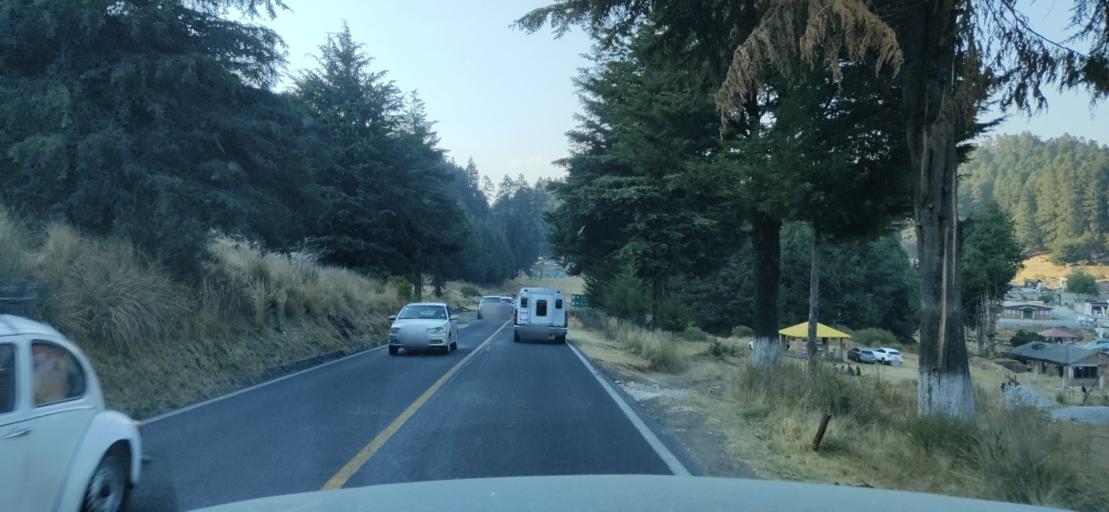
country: MX
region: Mexico
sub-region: Ocoyoacac
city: San Jeronimo Acazulco
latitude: 19.2786
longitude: -99.3808
